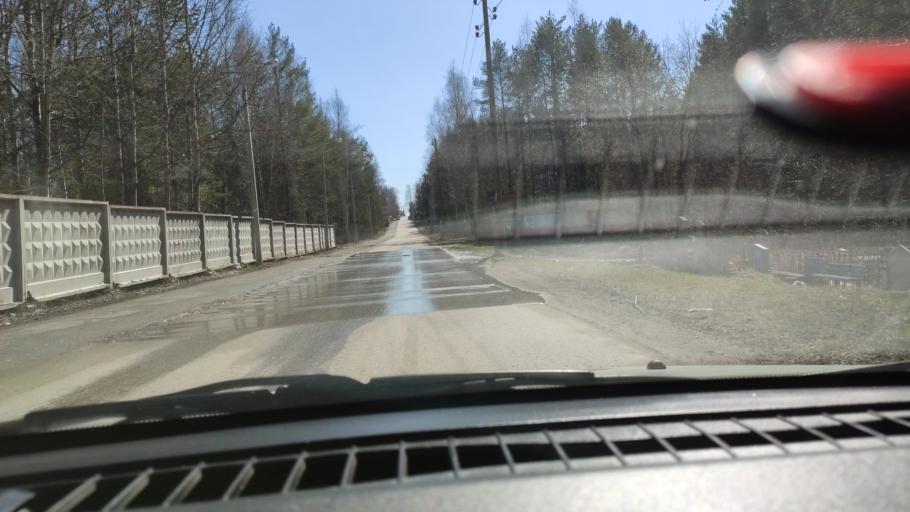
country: RU
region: Perm
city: Kondratovo
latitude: 58.0626
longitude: 56.1254
